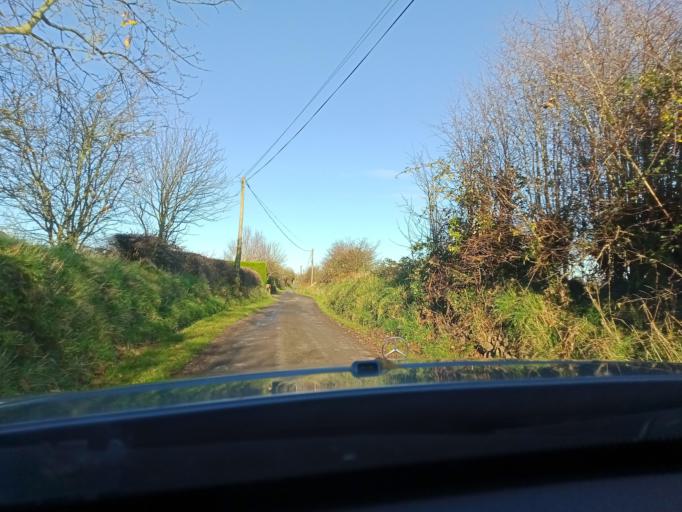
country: IE
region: Leinster
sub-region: Kilkenny
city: Mooncoin
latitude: 52.2938
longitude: -7.2082
